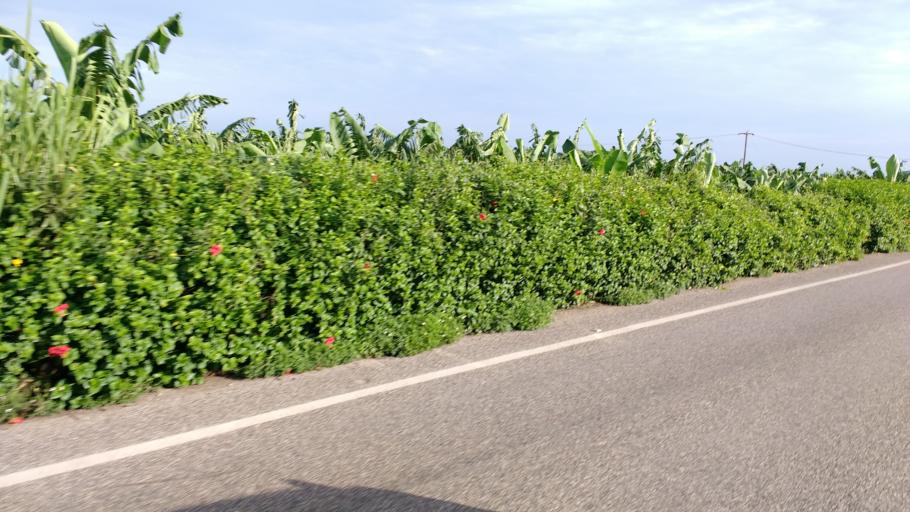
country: MX
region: Tabasco
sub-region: Teapa
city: Eureka y Belen
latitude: 17.6138
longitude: -92.9646
